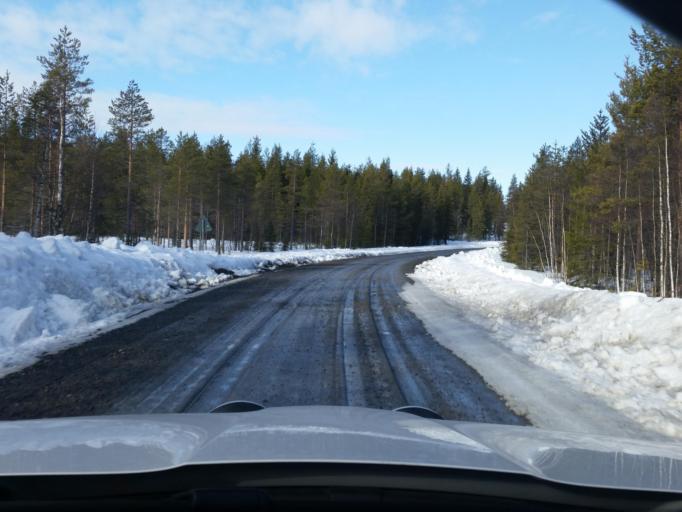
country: SE
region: Vaesterbotten
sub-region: Skelleftea Kommun
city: Storvik
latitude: 65.5086
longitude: 20.3183
